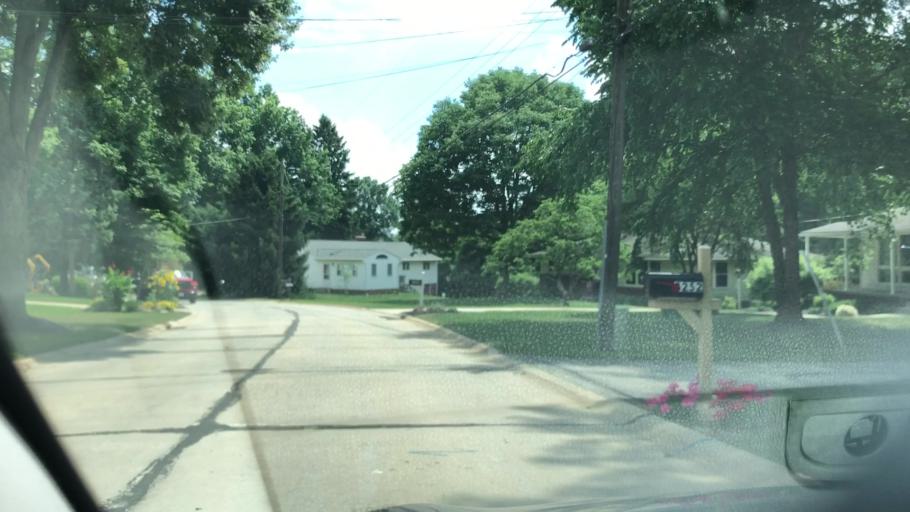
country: US
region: Ohio
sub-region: Summit County
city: Fairlawn
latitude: 41.1281
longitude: -81.6236
